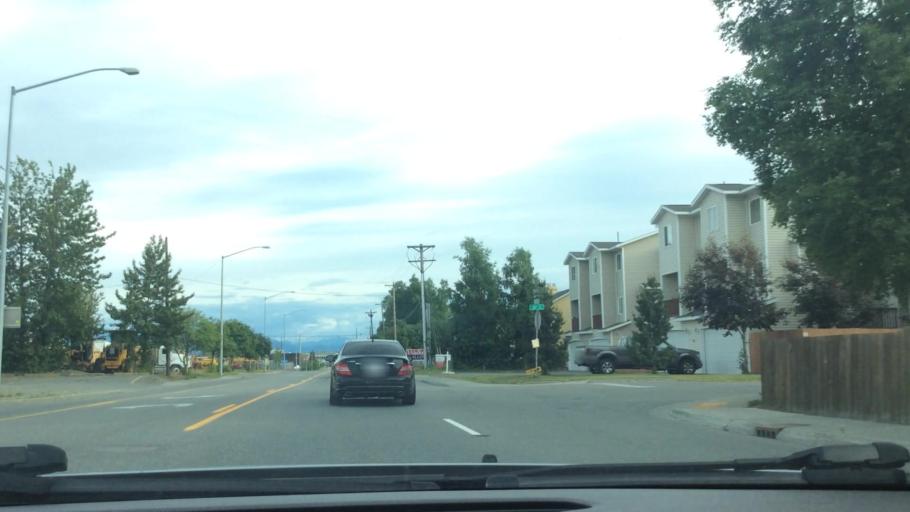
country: US
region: Alaska
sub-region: Anchorage Municipality
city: Anchorage
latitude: 61.1728
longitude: -149.8980
